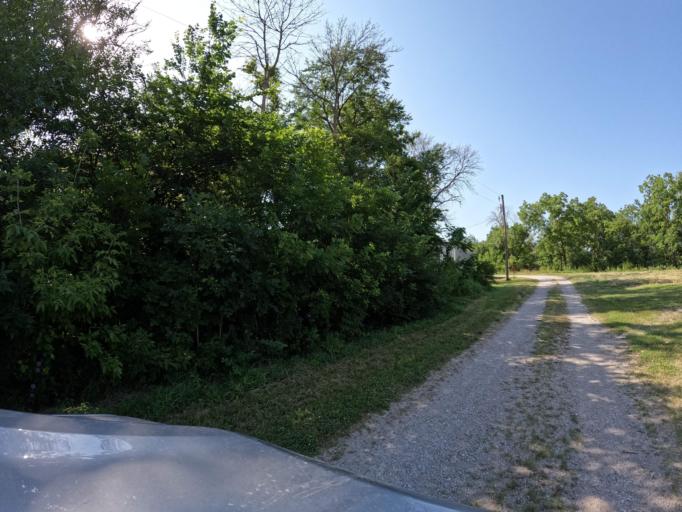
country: US
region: Iowa
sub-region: Appanoose County
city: Centerville
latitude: 40.7183
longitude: -93.0272
